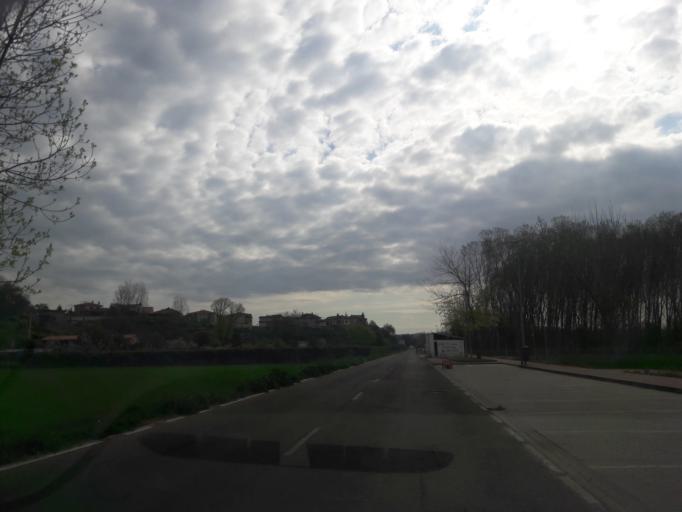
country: ES
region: Castille and Leon
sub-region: Provincia de Salamanca
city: Ciudad Rodrigo
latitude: 40.5936
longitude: -6.5300
